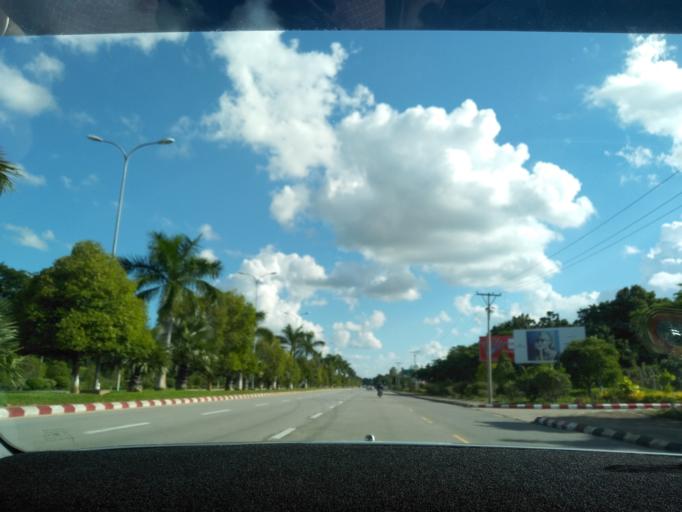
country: MM
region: Mandalay
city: Nay Pyi Taw
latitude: 19.7305
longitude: 96.1111
